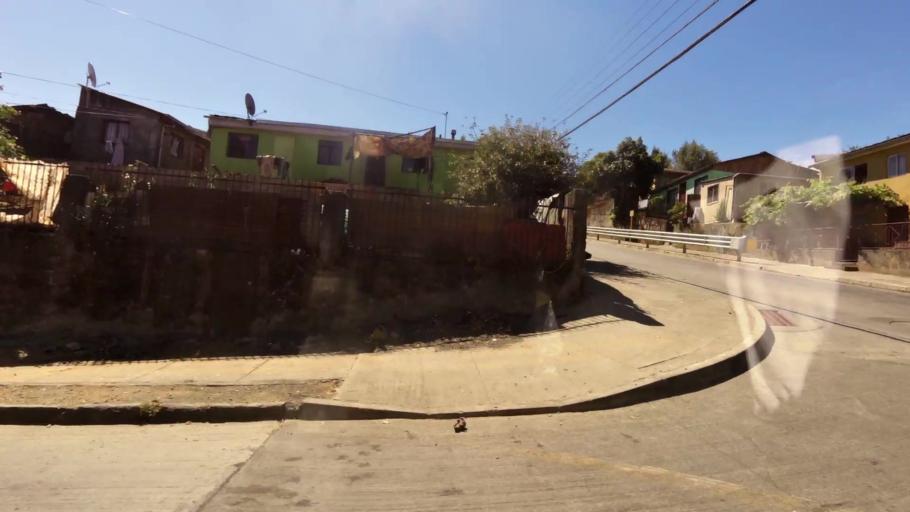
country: CL
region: Biobio
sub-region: Provincia de Concepcion
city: Penco
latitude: -36.7327
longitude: -72.9886
